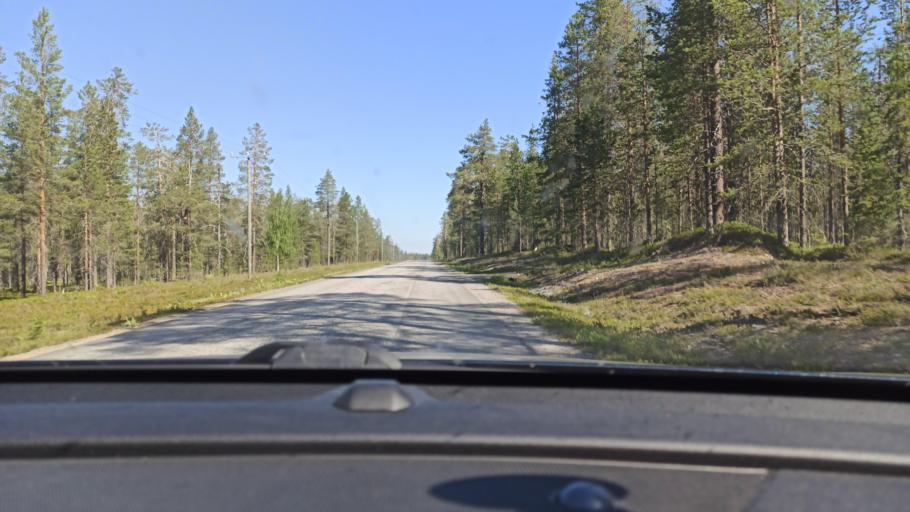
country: FI
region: Lapland
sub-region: Tunturi-Lappi
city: Kolari
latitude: 67.6405
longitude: 24.1577
